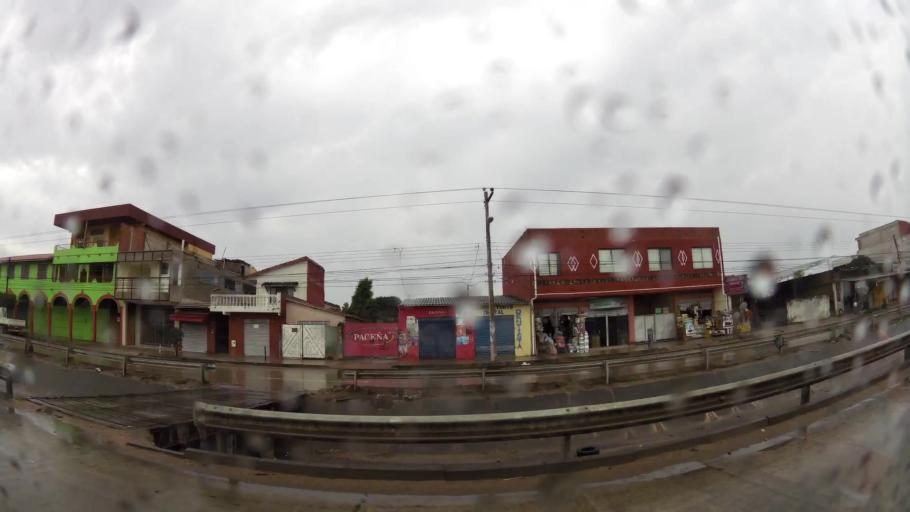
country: BO
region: Santa Cruz
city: Santa Cruz de la Sierra
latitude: -17.8015
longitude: -63.1342
